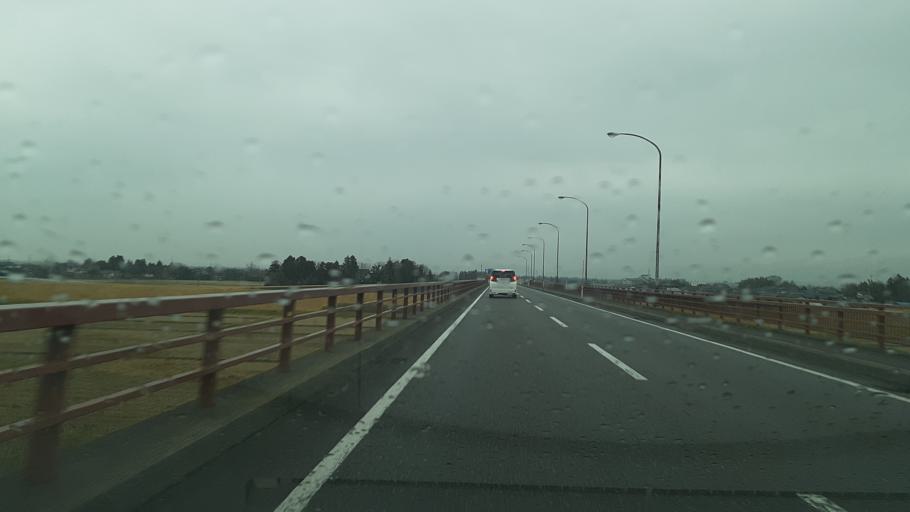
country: JP
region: Niigata
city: Kameda-honcho
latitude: 37.8804
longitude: 139.1673
